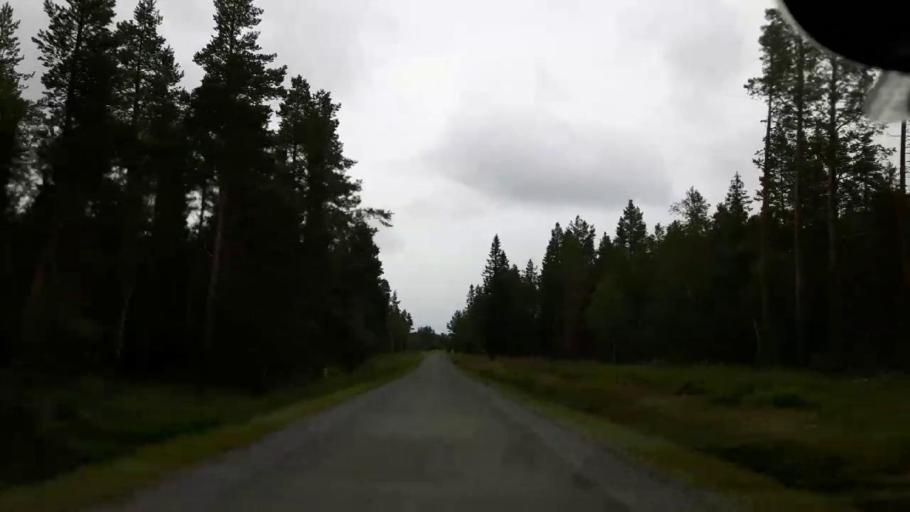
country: SE
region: Jaemtland
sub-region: OEstersunds Kommun
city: Ostersund
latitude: 63.0837
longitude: 14.5550
